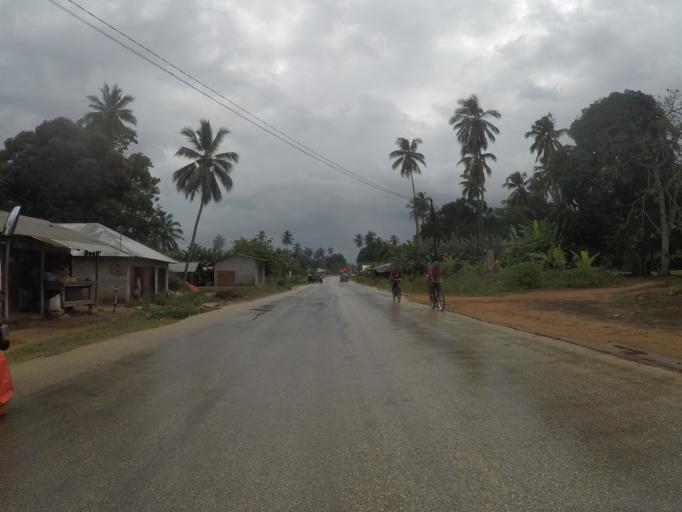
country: TZ
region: Zanzibar Central/South
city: Koani
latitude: -6.0461
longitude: 39.2272
